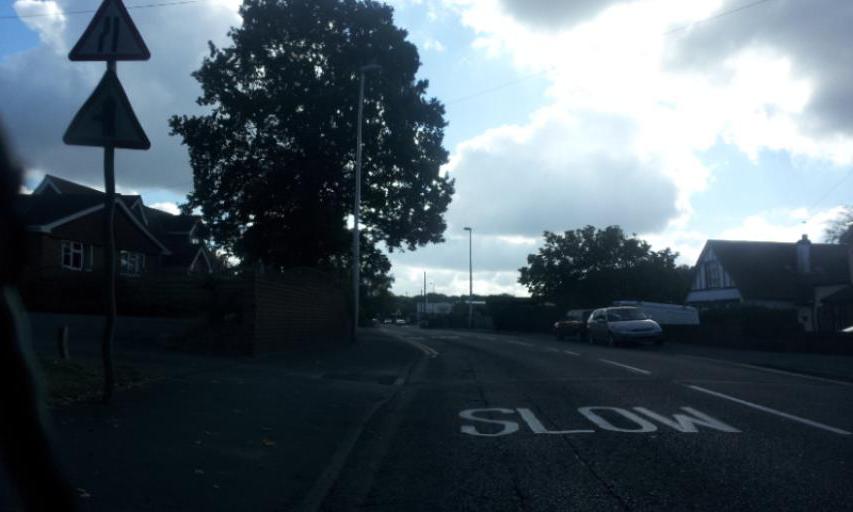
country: GB
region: England
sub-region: Kent
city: Rainham
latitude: 51.3551
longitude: 0.5797
